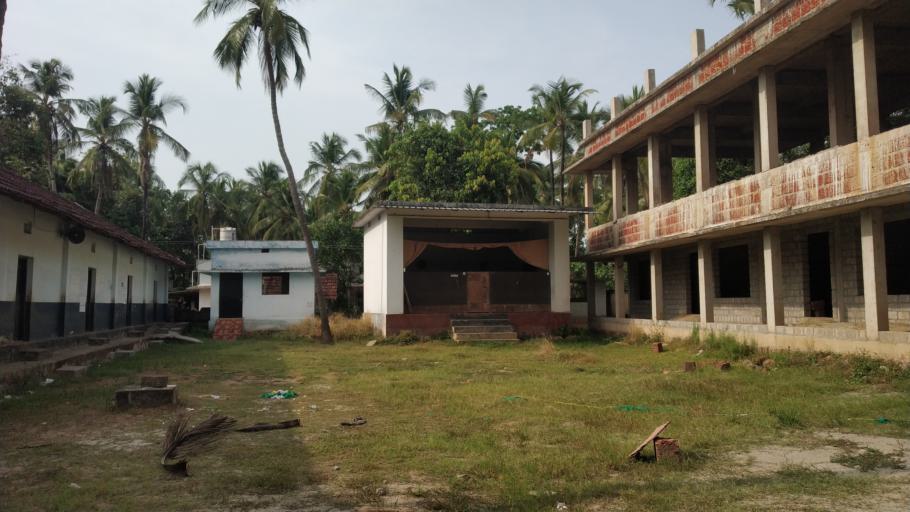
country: IN
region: Kerala
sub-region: Malappuram
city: Tirur
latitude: 10.8959
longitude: 75.9395
